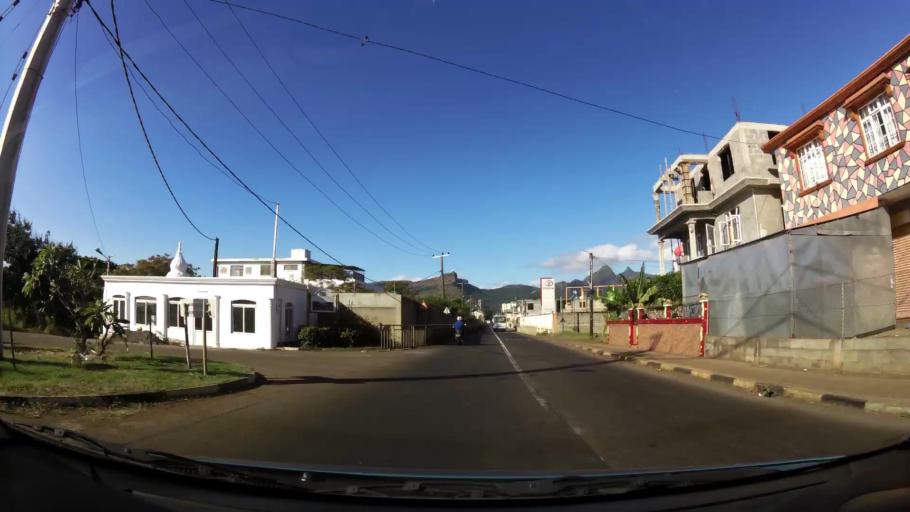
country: MU
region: Black River
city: Petite Riviere
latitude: -20.1836
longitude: 57.4638
